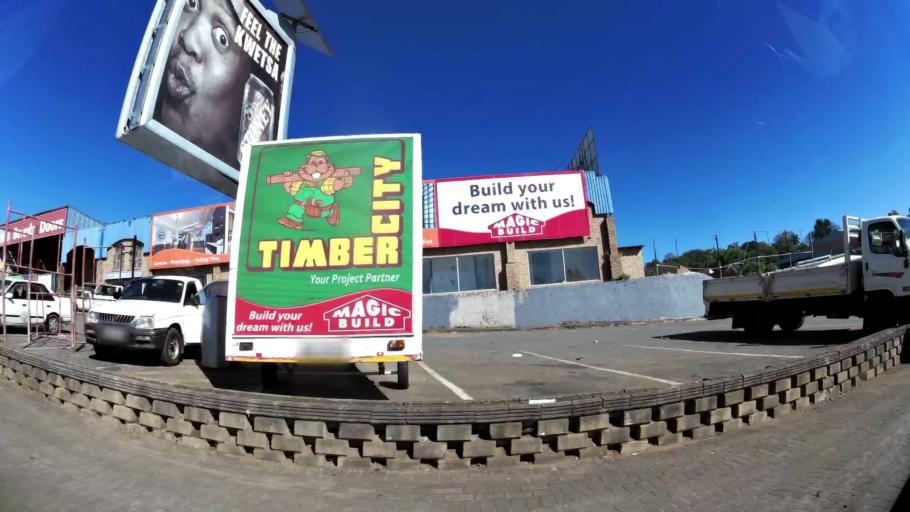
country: ZA
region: Limpopo
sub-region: Mopani District Municipality
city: Tzaneen
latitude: -23.8315
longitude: 30.1615
